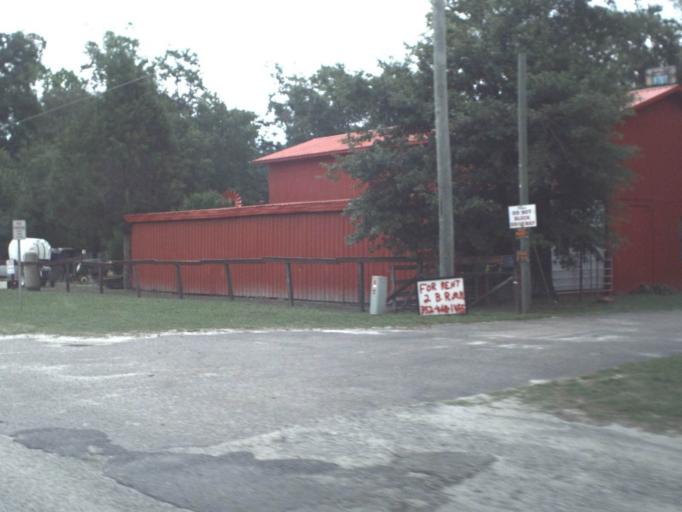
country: US
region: Florida
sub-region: Alachua County
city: Waldo
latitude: 29.8553
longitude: -82.1554
